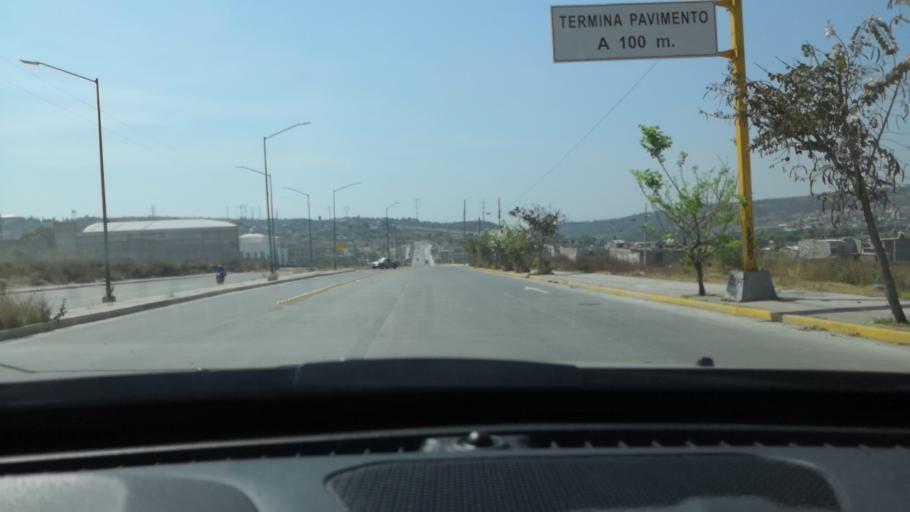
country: MX
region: Guanajuato
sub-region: Leon
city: Ejido la Joya
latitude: 21.1343
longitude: -101.7350
